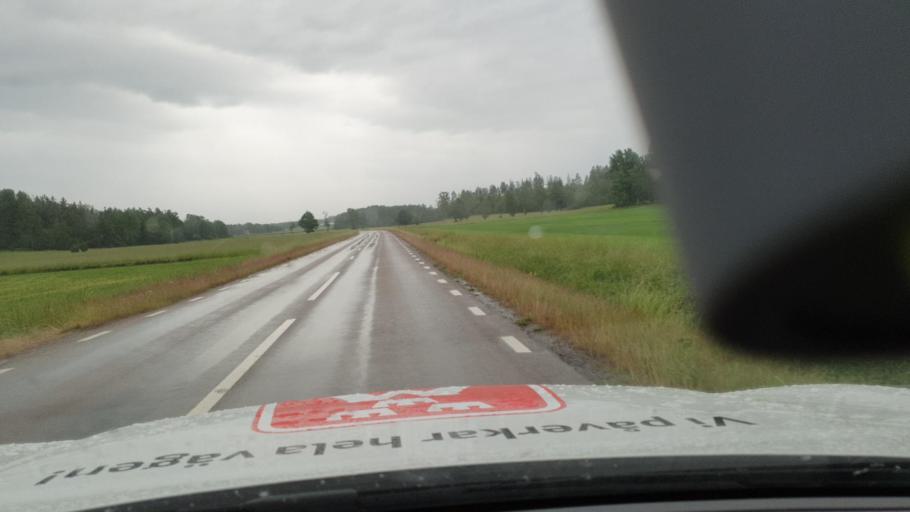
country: SE
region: Vaestra Goetaland
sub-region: Mariestads Kommun
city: Mariestad
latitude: 58.7735
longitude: 13.9068
